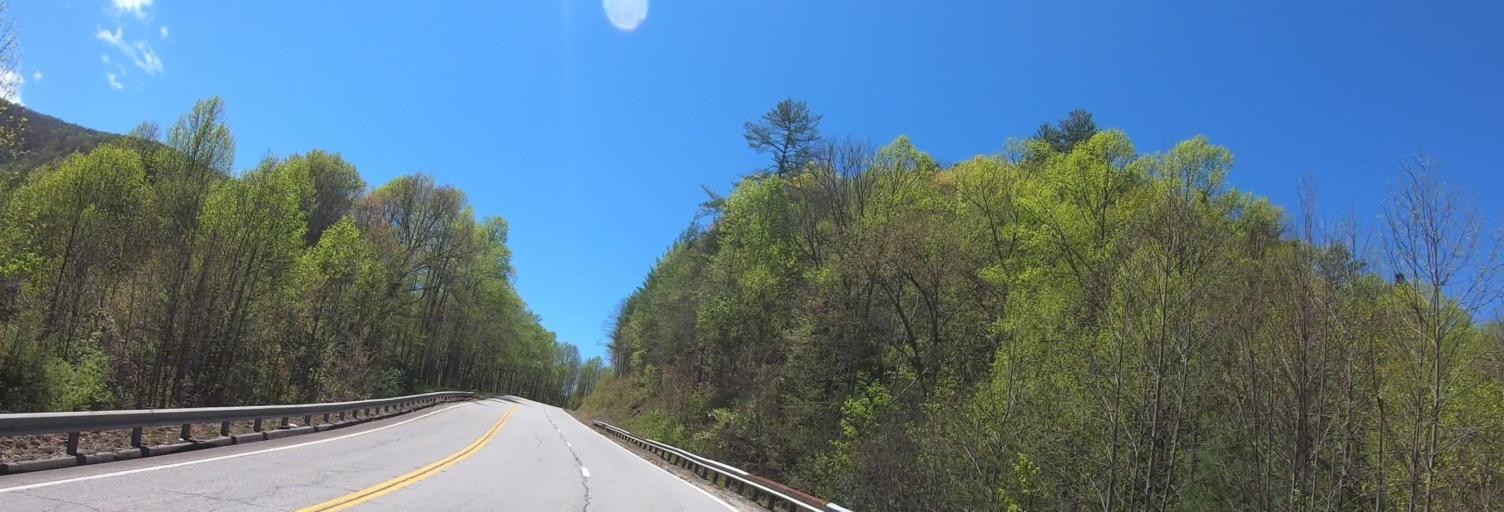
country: US
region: Georgia
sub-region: Towns County
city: Hiawassee
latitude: 34.8210
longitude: -83.7379
